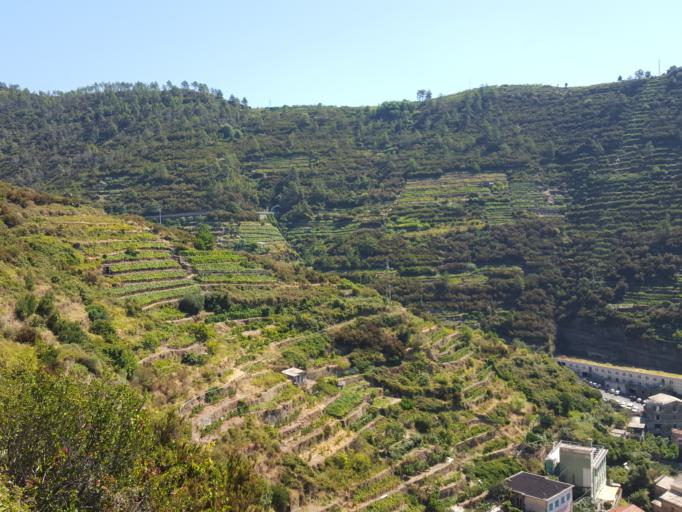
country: IT
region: Liguria
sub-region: Provincia di La Spezia
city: Riomaggiore
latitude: 44.1091
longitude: 9.7286
